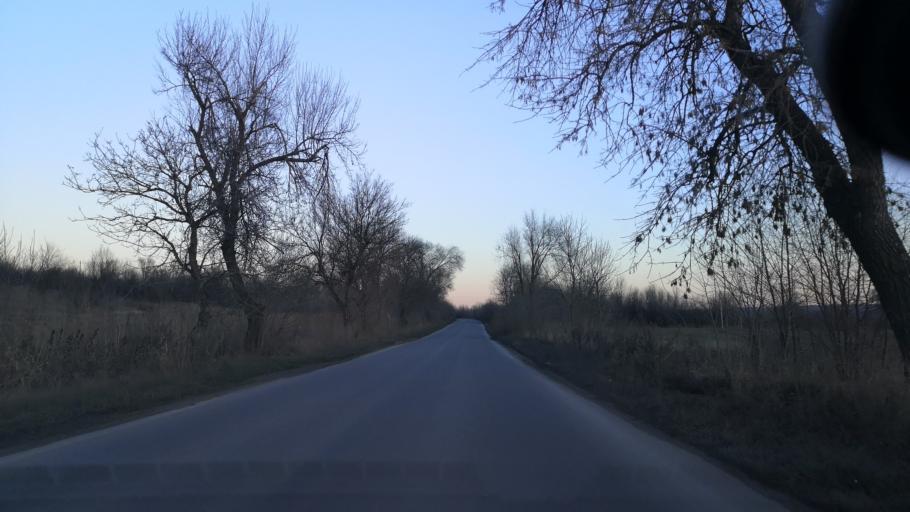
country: MD
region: Anenii Noi
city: Anenii Noi
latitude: 46.8882
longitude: 29.2628
